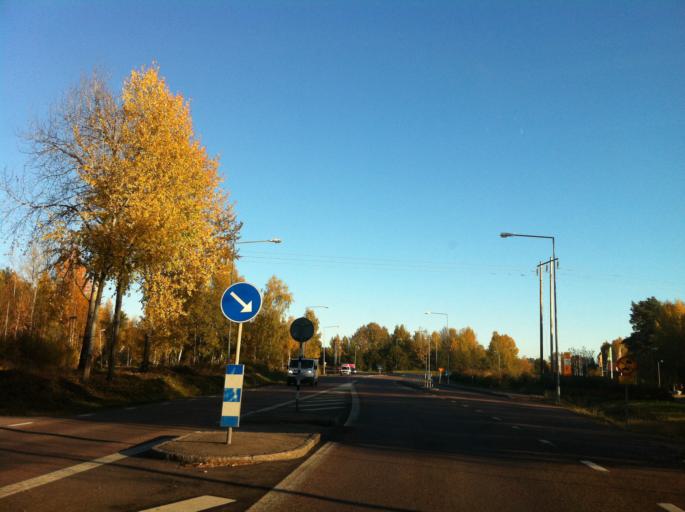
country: SE
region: Dalarna
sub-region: Faluns Kommun
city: Falun
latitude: 60.6267
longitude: 15.6080
